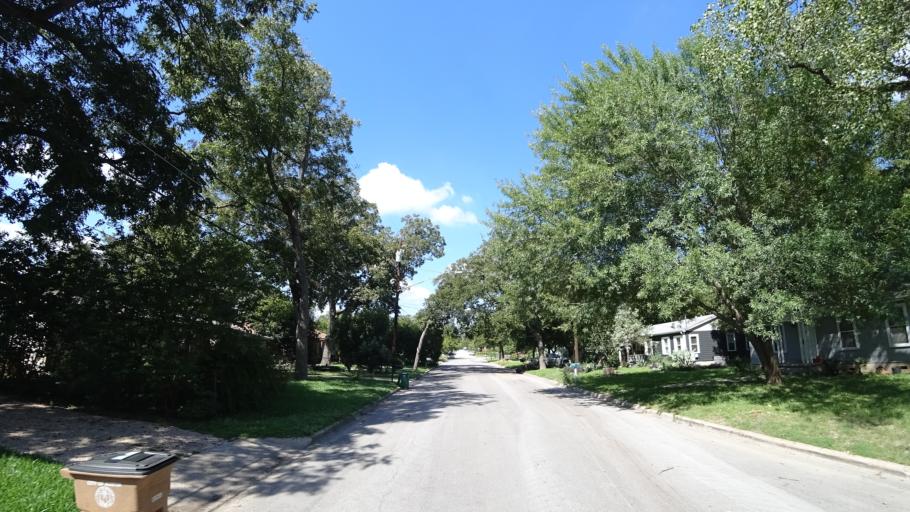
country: US
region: Texas
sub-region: Travis County
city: Austin
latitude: 30.3315
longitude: -97.7174
